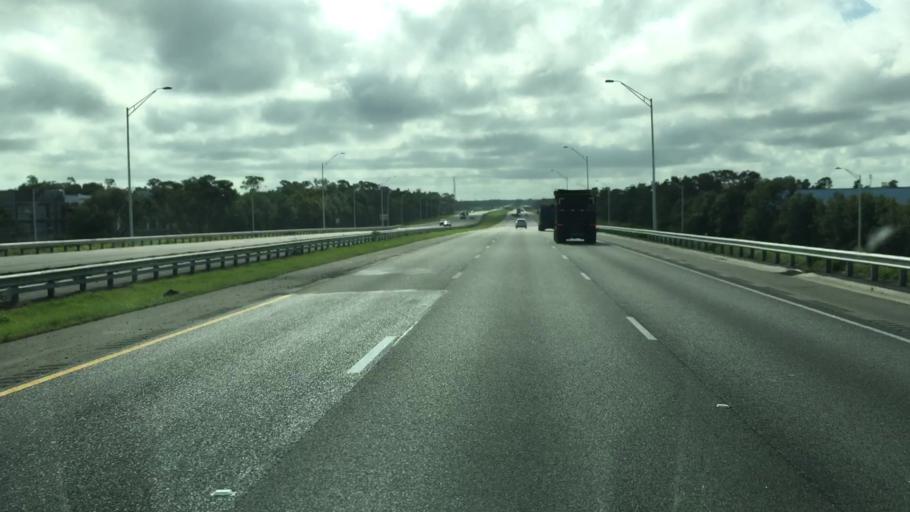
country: US
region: Florida
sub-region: Volusia County
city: Port Orange
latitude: 29.1044
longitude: -81.0280
